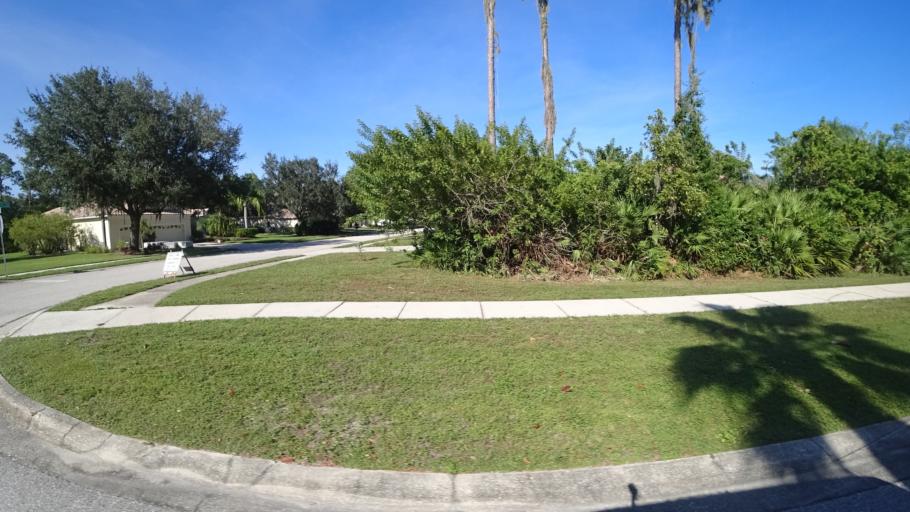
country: US
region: Florida
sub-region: Sarasota County
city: The Meadows
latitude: 27.4032
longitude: -82.4351
